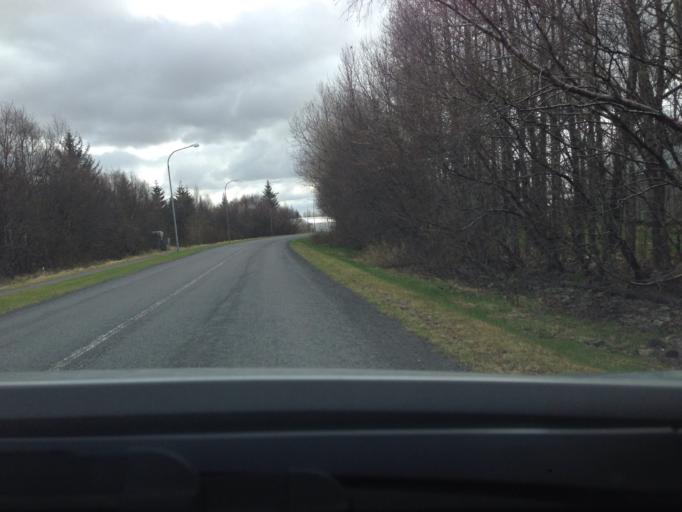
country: IS
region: South
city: Selfoss
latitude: 64.1176
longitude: -20.5008
